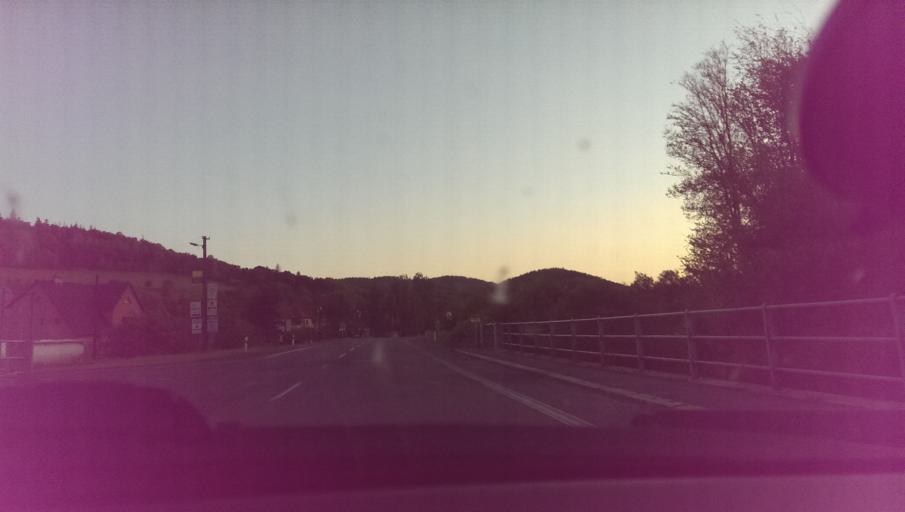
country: CZ
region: Zlin
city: Jablunka
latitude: 49.4191
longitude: 17.9597
